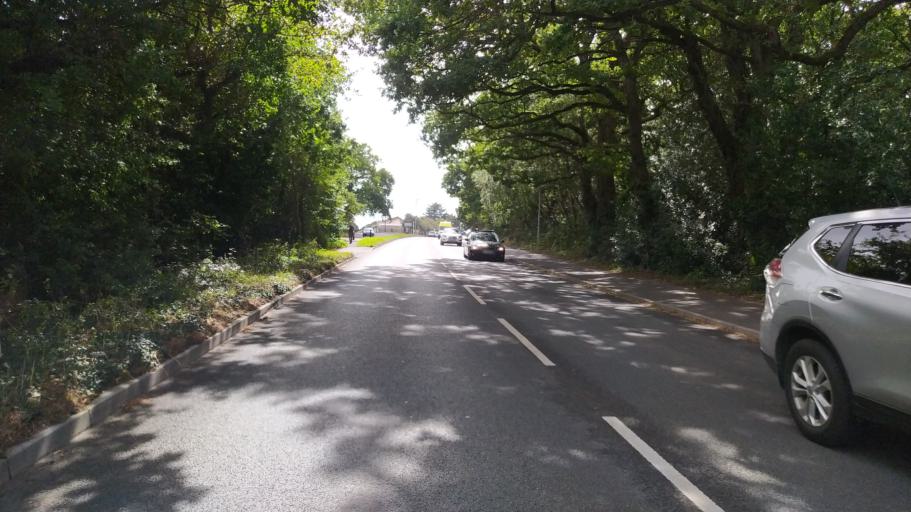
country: GB
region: England
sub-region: Dorset
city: Wareham
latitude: 50.6997
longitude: -2.1084
